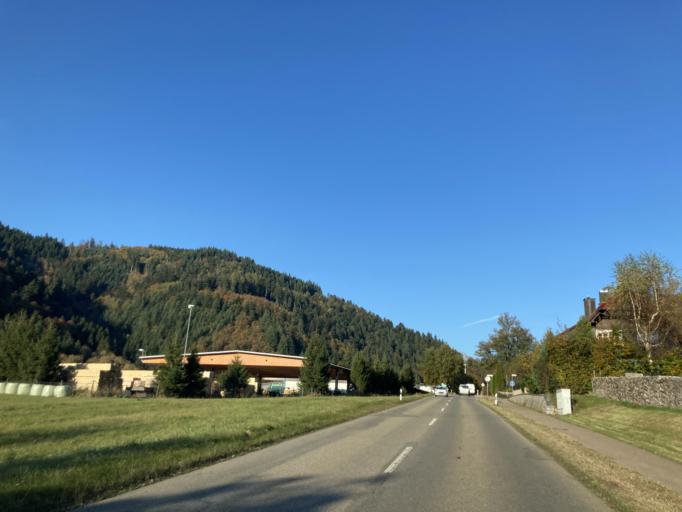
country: DE
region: Baden-Wuerttemberg
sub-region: Freiburg Region
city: Buchenbach
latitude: 47.9671
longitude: 8.0273
